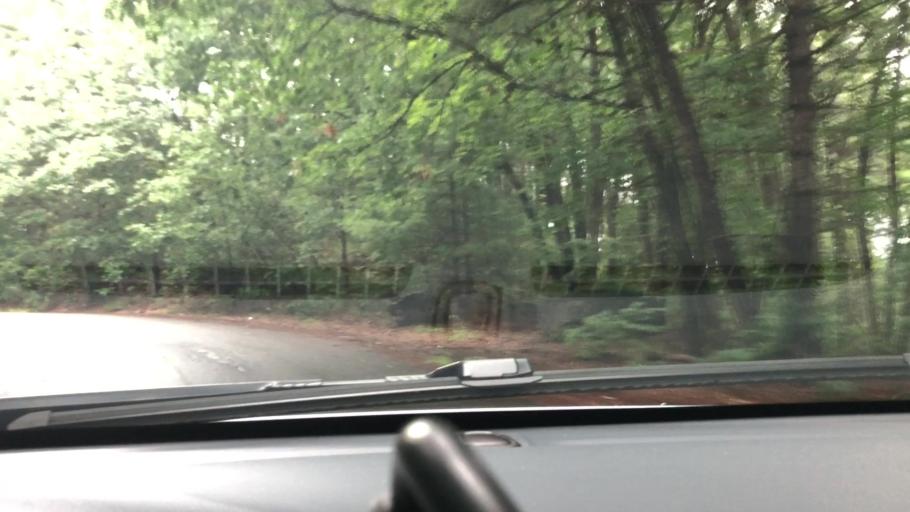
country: US
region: New Hampshire
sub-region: Hillsborough County
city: Pinardville
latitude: 43.0012
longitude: -71.4986
